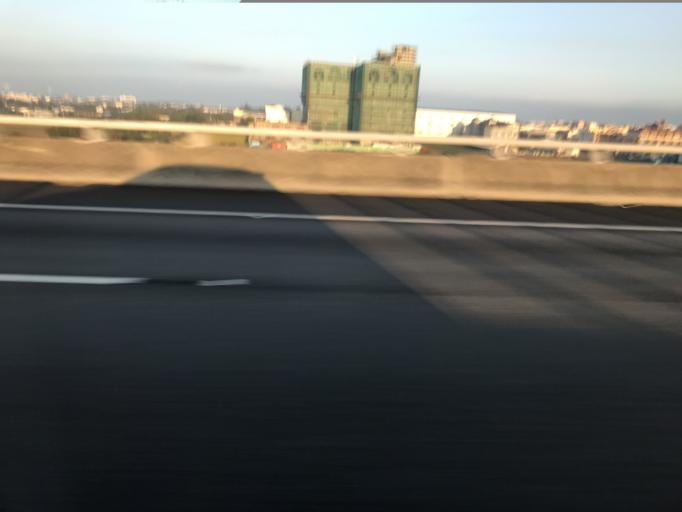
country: TW
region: Taiwan
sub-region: Miaoli
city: Miaoli
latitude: 24.6154
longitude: 120.8098
